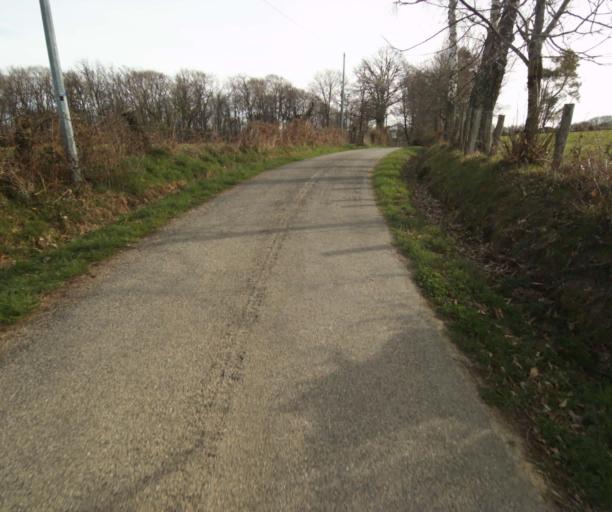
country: FR
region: Limousin
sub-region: Departement de la Correze
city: Chamboulive
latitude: 45.4370
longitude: 1.7397
